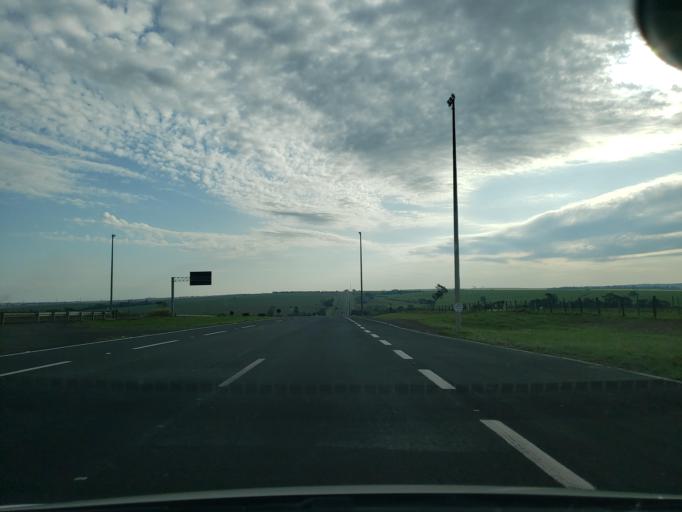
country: BR
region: Sao Paulo
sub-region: Guararapes
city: Guararapes
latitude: -21.2101
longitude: -50.7330
